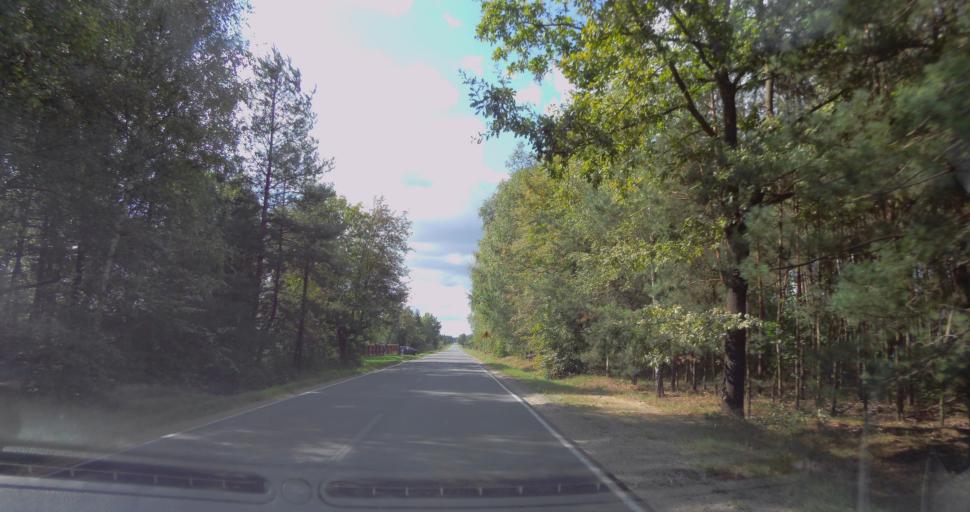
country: PL
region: Subcarpathian Voivodeship
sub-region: Powiat tarnobrzeski
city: Nowa Deba
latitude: 50.4017
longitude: 21.7972
